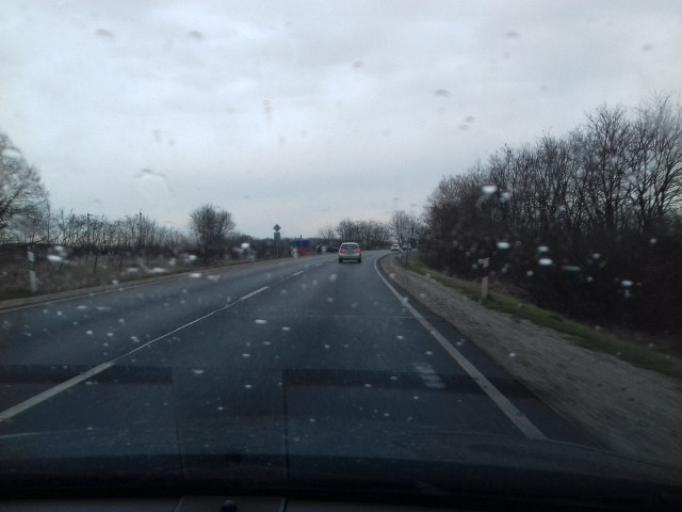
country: HU
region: Szabolcs-Szatmar-Bereg
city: Ujfeherto
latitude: 47.8393
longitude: 21.7047
